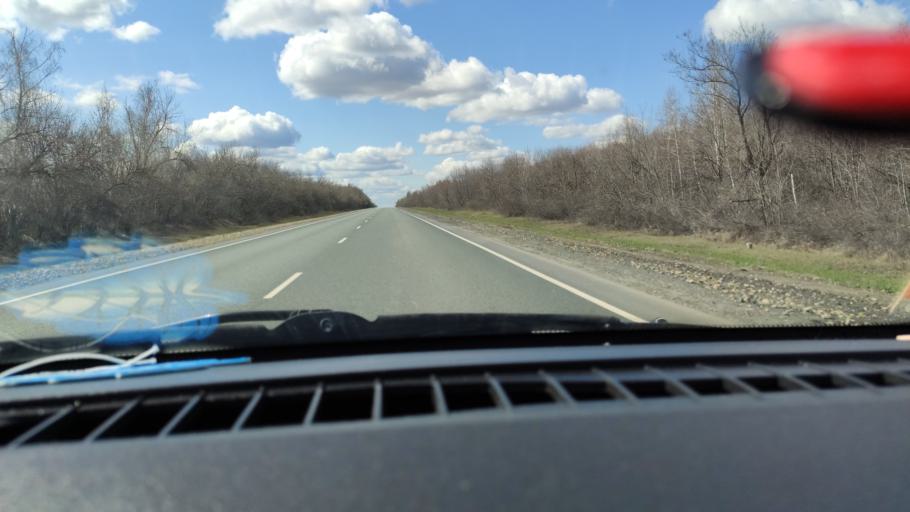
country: RU
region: Saratov
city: Khvalynsk
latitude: 52.6011
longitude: 48.1450
